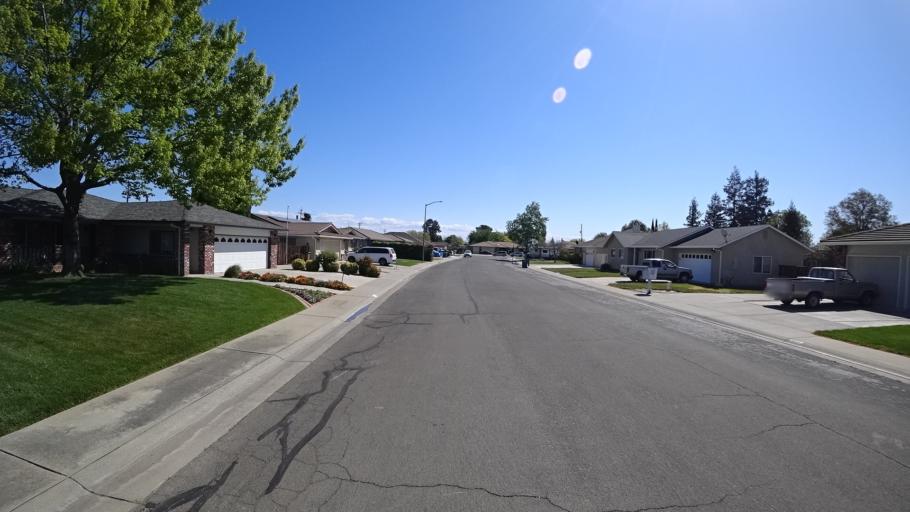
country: US
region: California
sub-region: Glenn County
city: Orland
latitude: 39.7541
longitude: -122.2027
